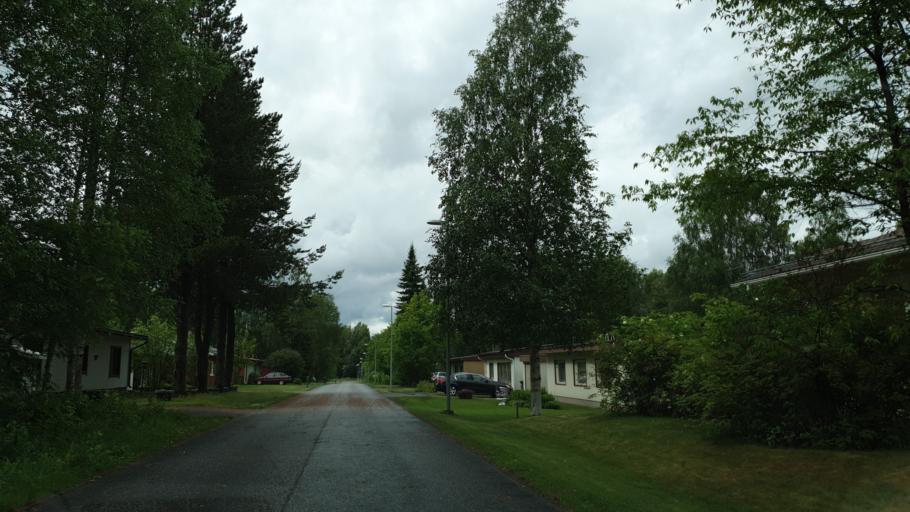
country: FI
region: Kainuu
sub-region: Kehys-Kainuu
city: Kuhmo
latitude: 64.1189
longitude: 29.5108
